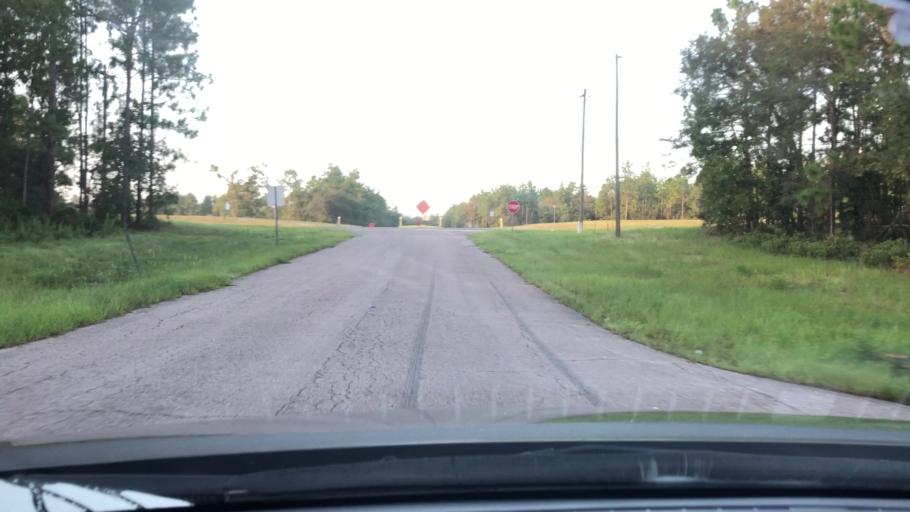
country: US
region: Florida
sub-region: Marion County
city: Belleview
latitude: 29.0269
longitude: -82.2403
